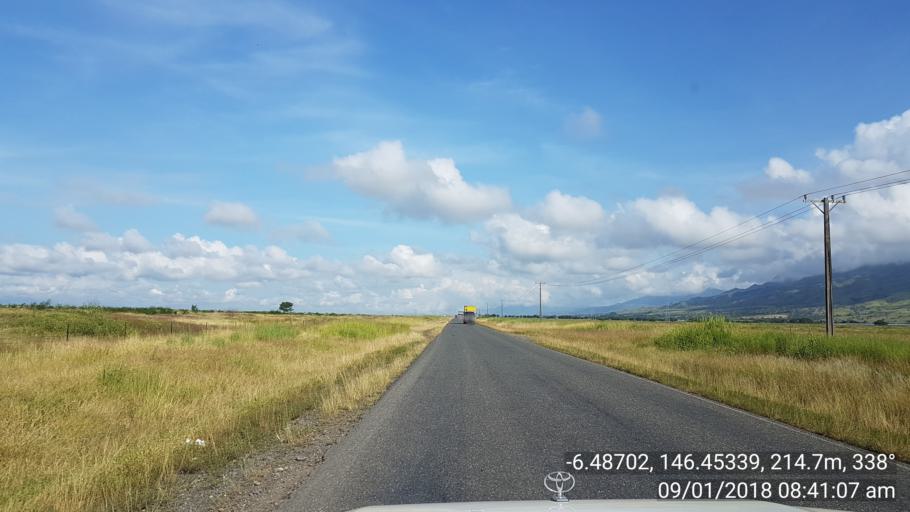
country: PG
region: Morobe
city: Lae
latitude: -6.4872
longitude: 146.4538
